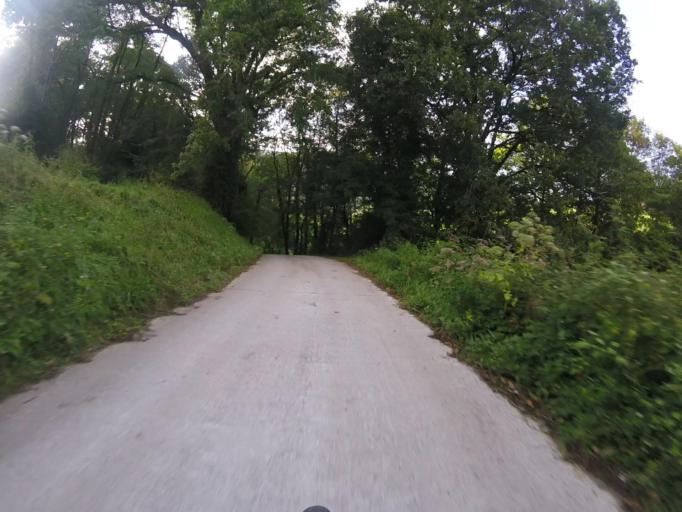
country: ES
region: Basque Country
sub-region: Provincia de Guipuzcoa
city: Fuenterrabia
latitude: 43.3512
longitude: -1.8195
